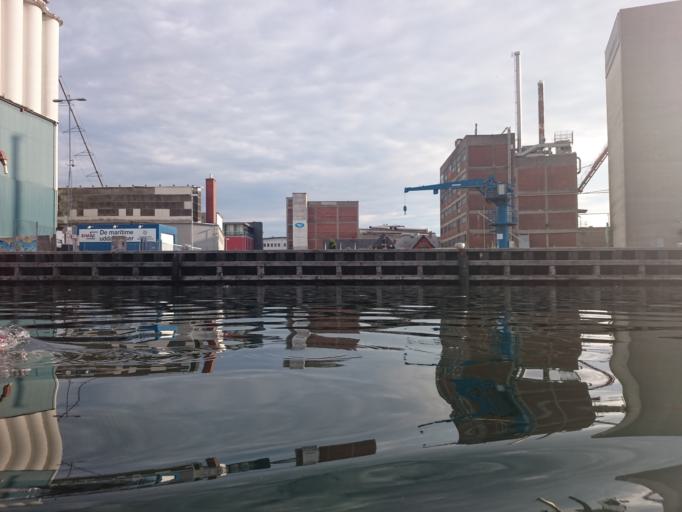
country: DK
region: South Denmark
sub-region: Svendborg Kommune
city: Svendborg
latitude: 55.0601
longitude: 10.6210
